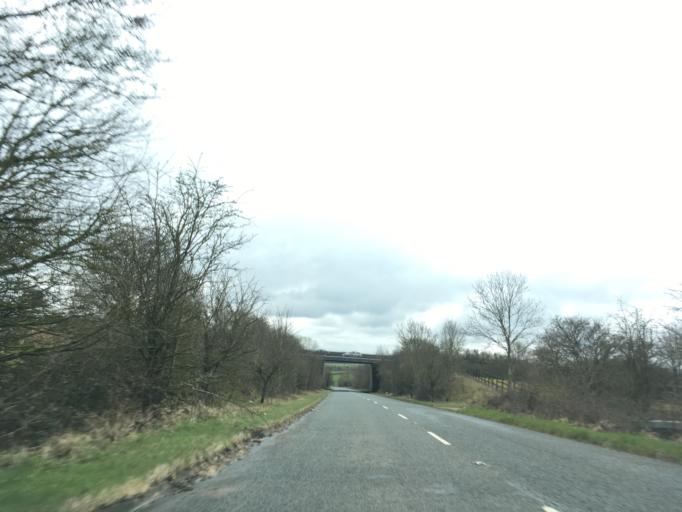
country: GB
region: England
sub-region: West Berkshire
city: Lambourn
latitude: 51.4731
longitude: -1.5289
